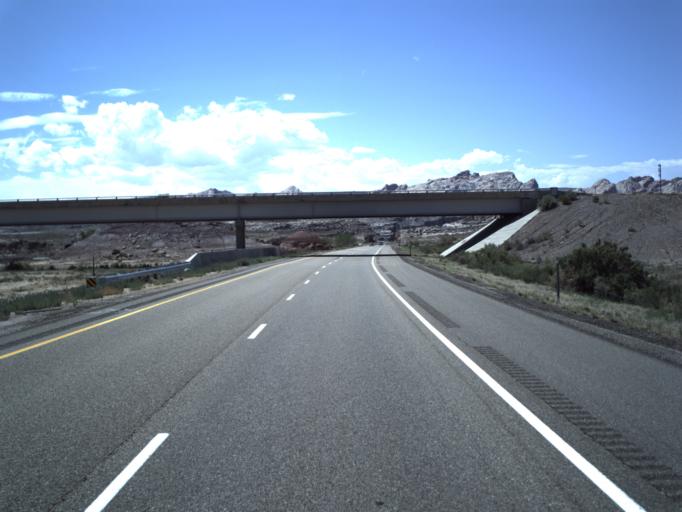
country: US
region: Utah
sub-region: Carbon County
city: East Carbon City
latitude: 38.9236
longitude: -110.3752
